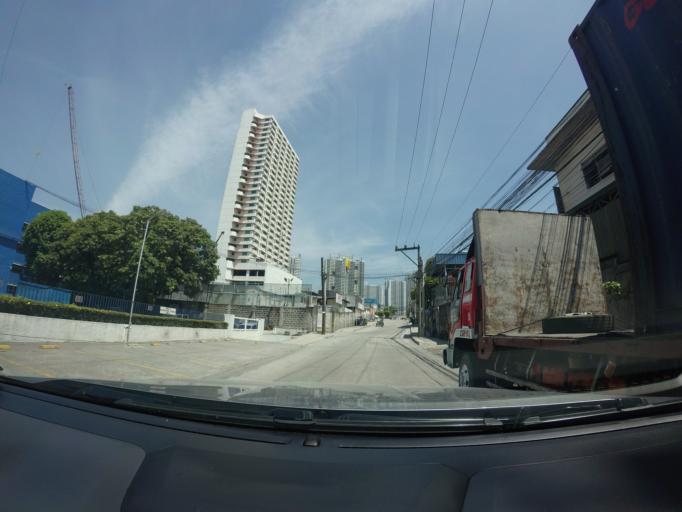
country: PH
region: Metro Manila
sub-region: Pasig
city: Pasig City
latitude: 14.5715
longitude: 121.0552
